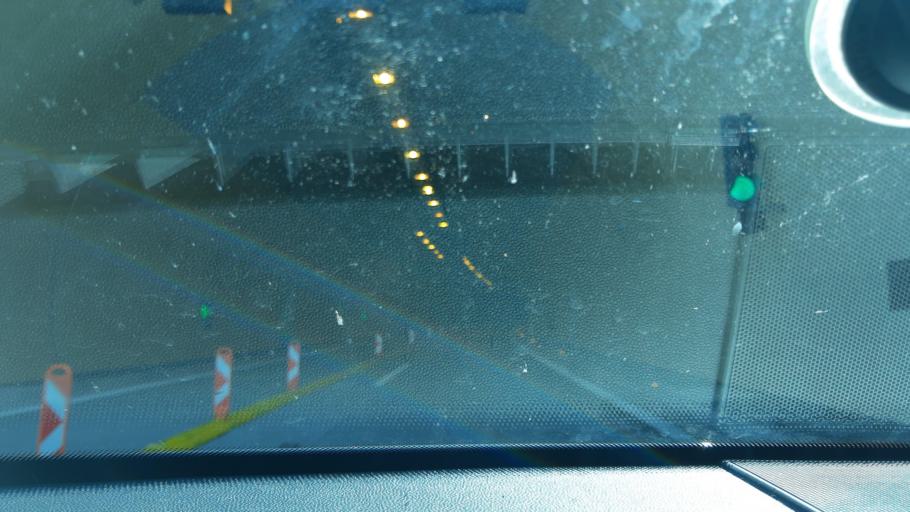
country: SK
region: Zilinsky
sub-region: Okres Zilina
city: Zilina
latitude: 49.1888
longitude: 18.7113
